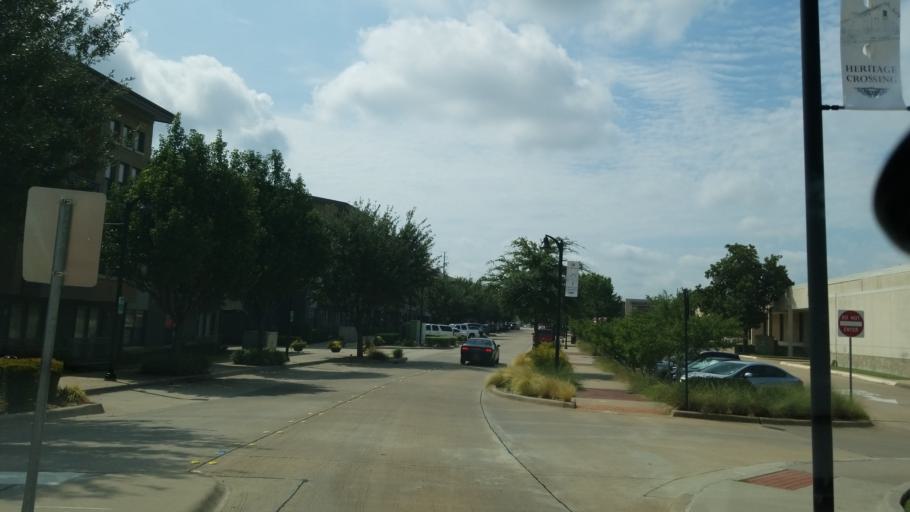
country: US
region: Texas
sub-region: Dallas County
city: Garland
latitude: 32.9155
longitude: -96.6378
